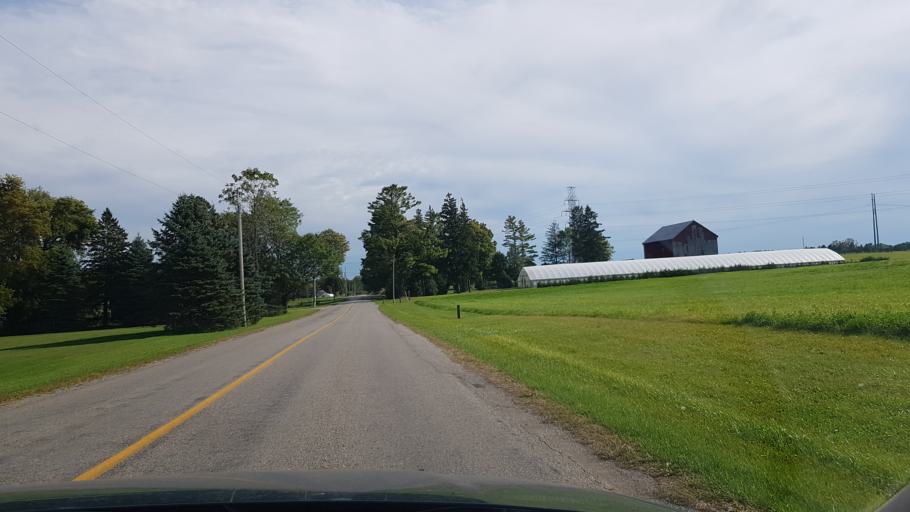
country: CA
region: Ontario
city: Delaware
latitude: 42.8963
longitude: -81.4707
